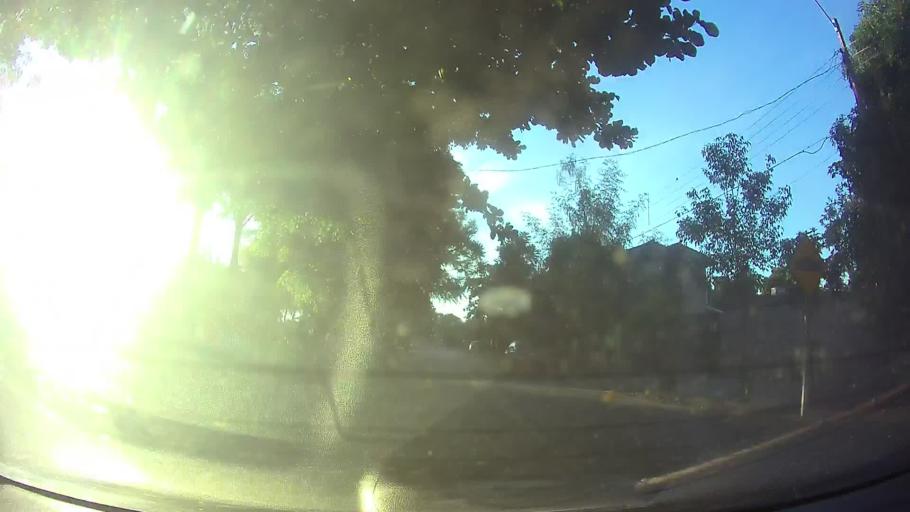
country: PY
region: Central
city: San Lorenzo
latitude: -25.2723
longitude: -57.5015
